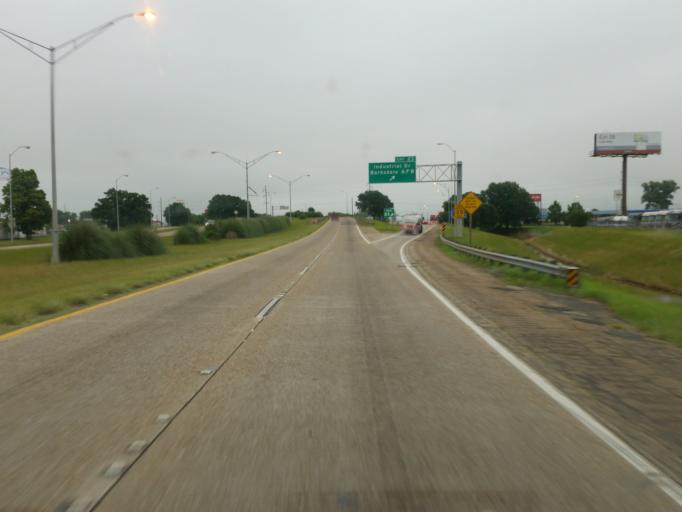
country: US
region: Louisiana
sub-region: Bossier Parish
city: Bossier City
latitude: 32.5275
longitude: -93.6782
